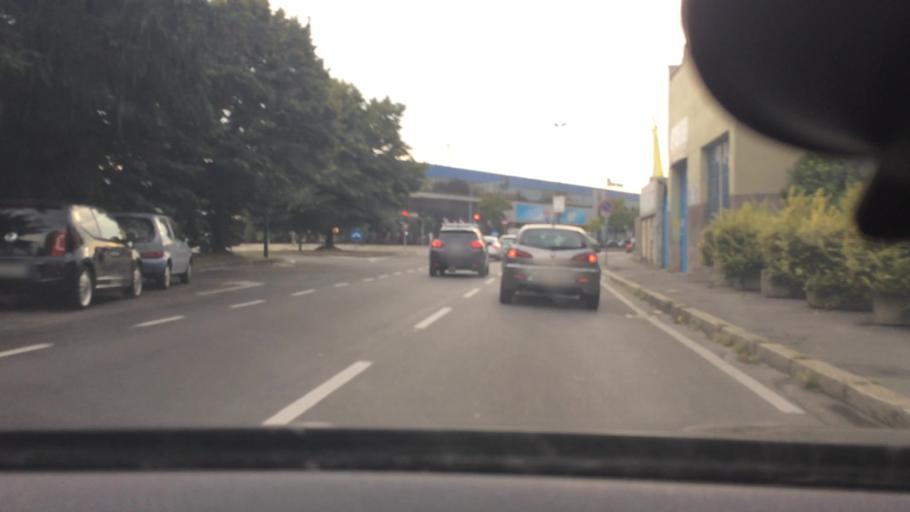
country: IT
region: Lombardy
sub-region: Citta metropolitana di Milano
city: Sesto San Giovanni
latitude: 45.5308
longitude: 9.2244
